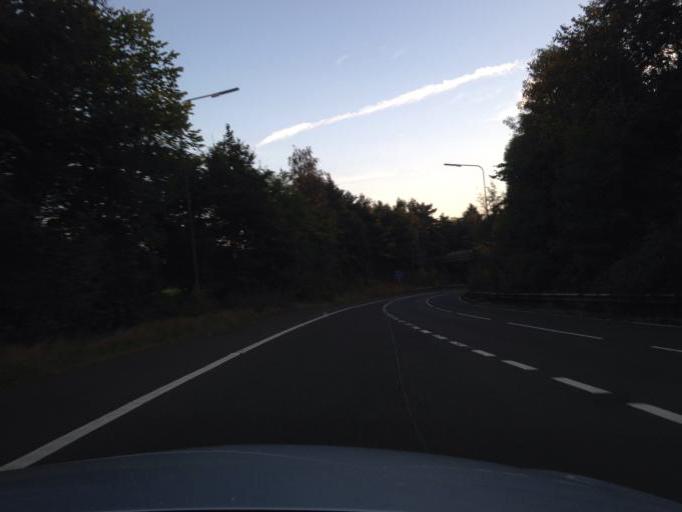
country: GB
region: England
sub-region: Manchester
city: Didsbury
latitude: 53.3976
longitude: -2.2213
